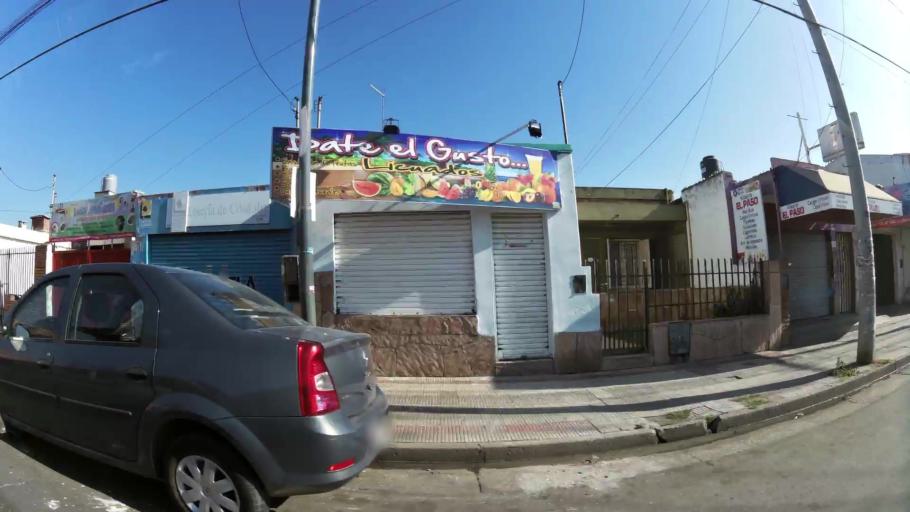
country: AR
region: Cordoba
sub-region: Departamento de Capital
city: Cordoba
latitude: -31.4757
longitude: -64.2200
